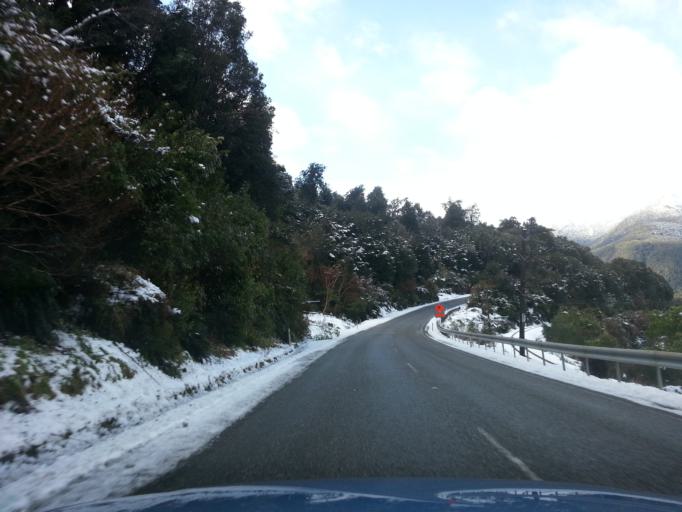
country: NZ
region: West Coast
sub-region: Grey District
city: Greymouth
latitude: -42.7965
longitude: 171.5822
